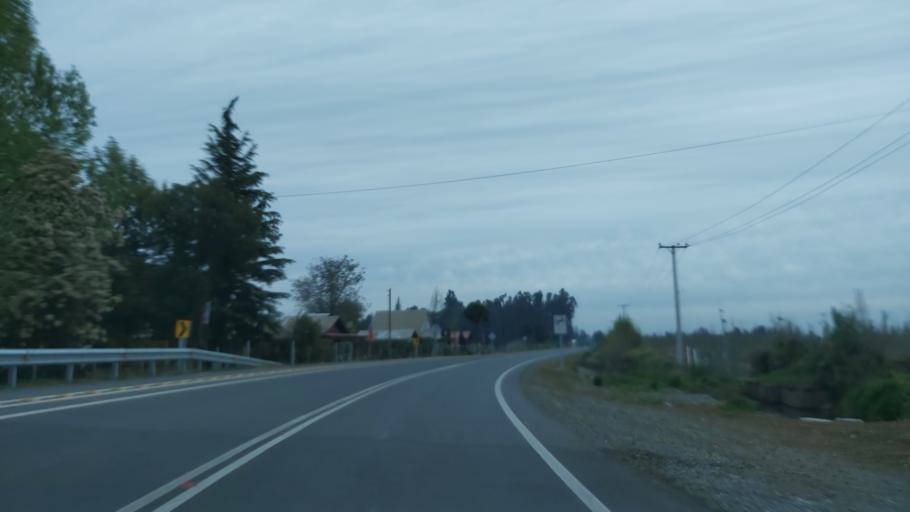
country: CL
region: Maule
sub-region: Provincia de Linares
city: Colbun
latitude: -35.7086
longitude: -71.4811
